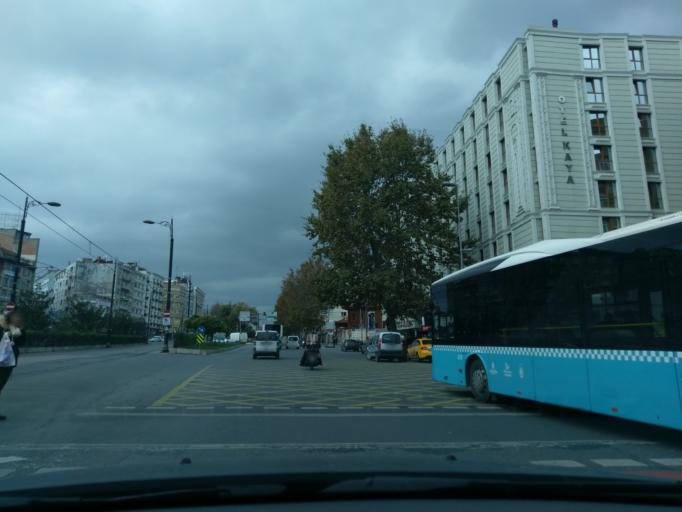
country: TR
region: Istanbul
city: Istanbul
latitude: 41.0120
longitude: 28.9401
